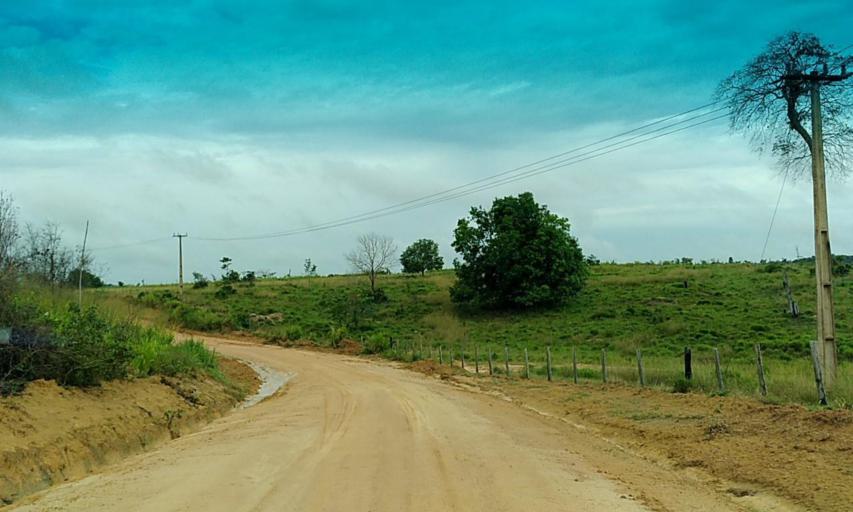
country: BR
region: Para
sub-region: Senador Jose Porfirio
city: Senador Jose Porfirio
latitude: -3.0410
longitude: -51.6782
